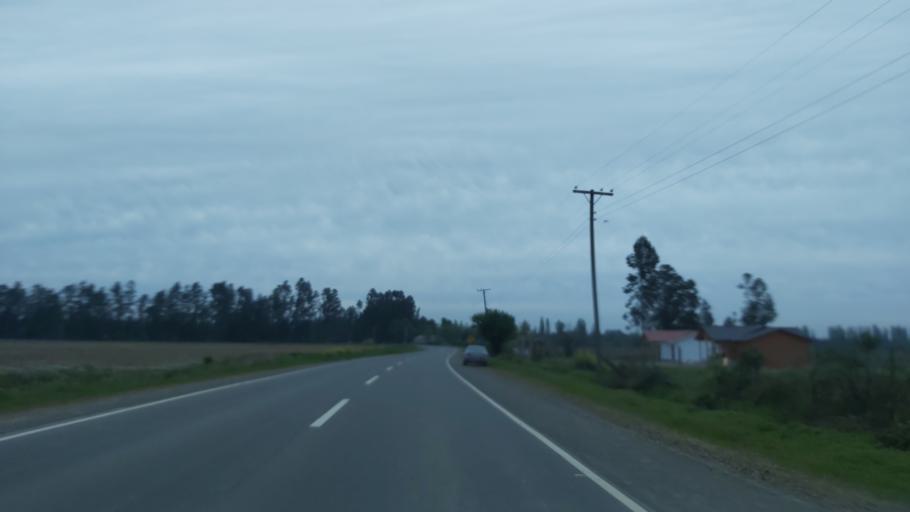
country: CL
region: Maule
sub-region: Provincia de Linares
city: Linares
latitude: -35.7782
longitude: -71.5175
